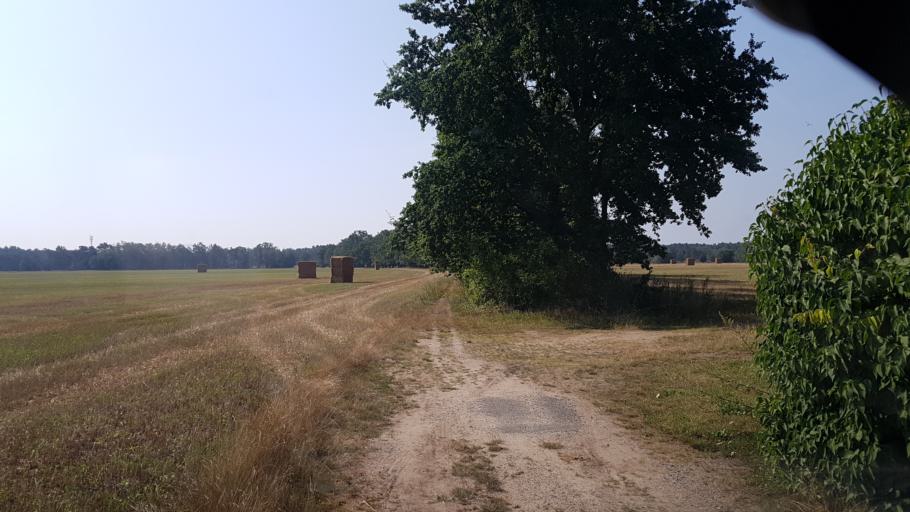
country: DE
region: Brandenburg
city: Cottbus
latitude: 51.7142
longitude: 14.4158
